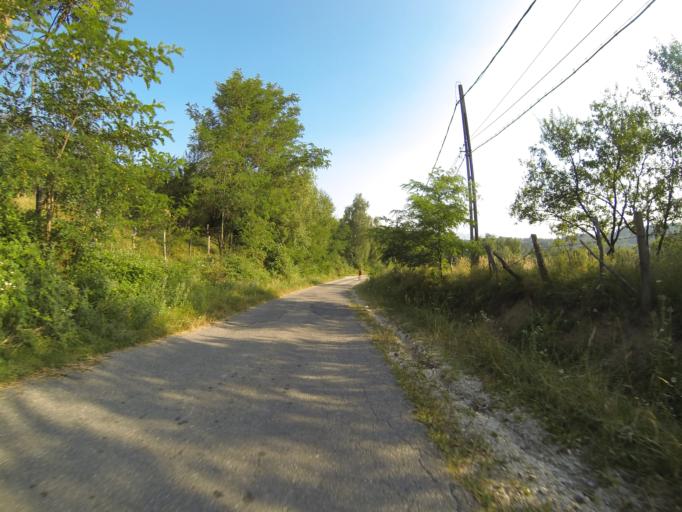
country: RO
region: Valcea
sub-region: Comuna Horezu
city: Horezu
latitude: 45.1742
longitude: 23.9879
